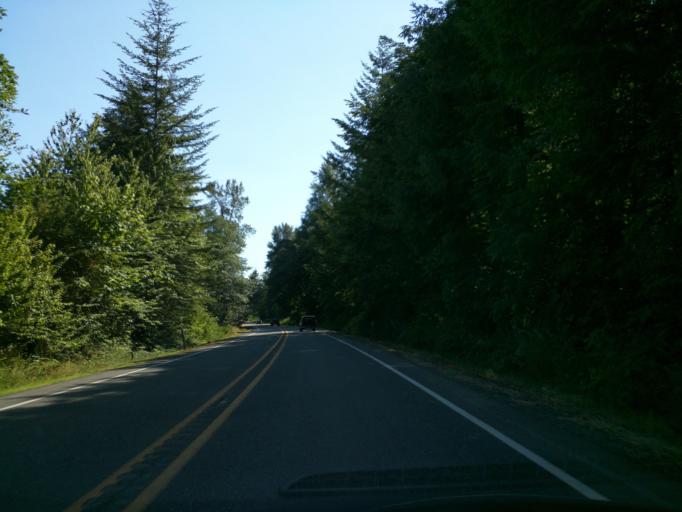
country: US
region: Washington
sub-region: Whatcom County
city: Peaceful Valley
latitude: 48.8480
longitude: -122.1621
